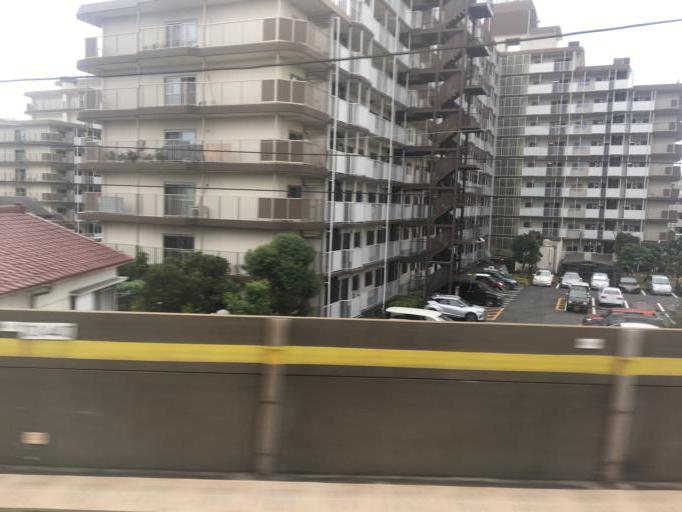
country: JP
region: Chiba
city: Funabashi
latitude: 35.7101
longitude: 139.9520
